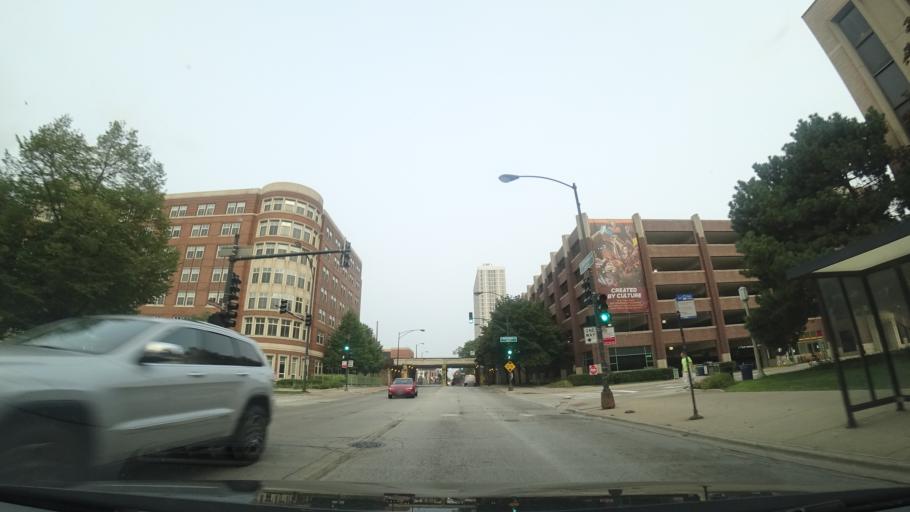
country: US
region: Illinois
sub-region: Cook County
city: Evanston
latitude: 41.9983
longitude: -87.6585
